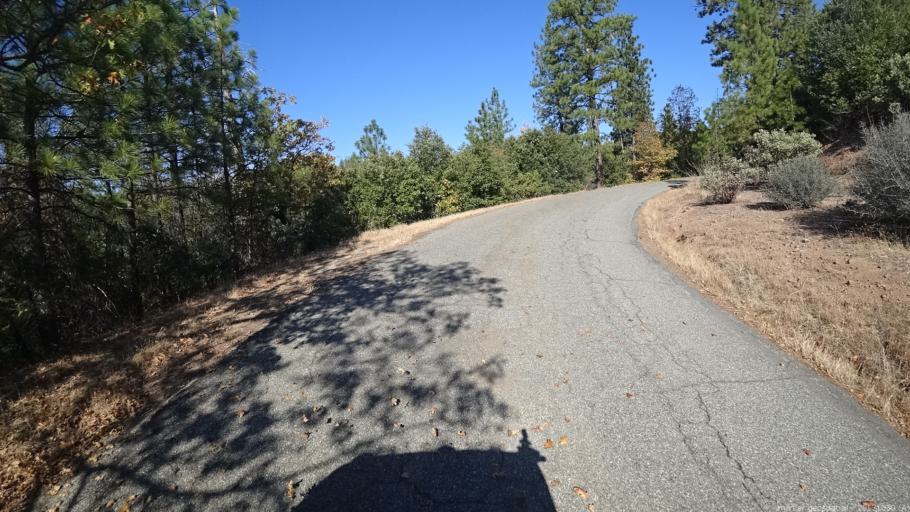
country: US
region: California
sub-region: Shasta County
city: Shingletown
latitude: 40.5763
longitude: -121.8791
